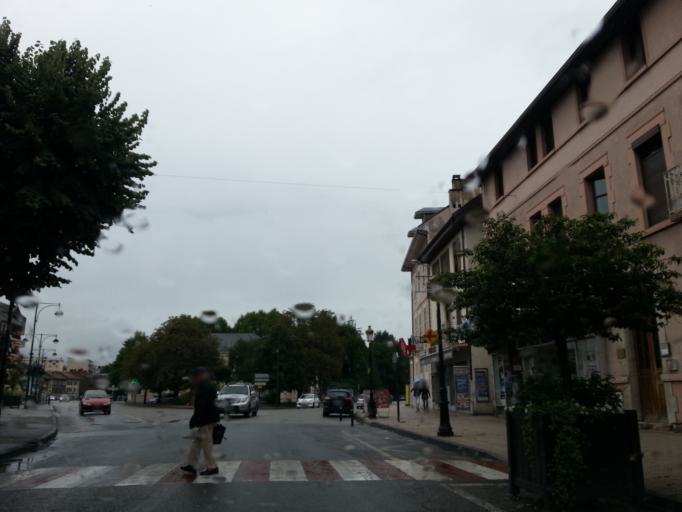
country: FR
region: Rhone-Alpes
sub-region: Departement de la Savoie
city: Albertville
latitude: 45.6753
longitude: 6.3888
